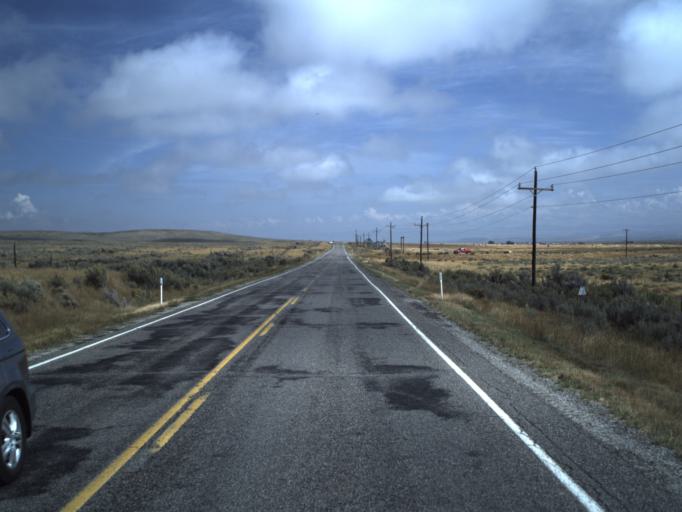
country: US
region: Utah
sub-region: Rich County
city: Randolph
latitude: 41.7471
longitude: -111.1479
